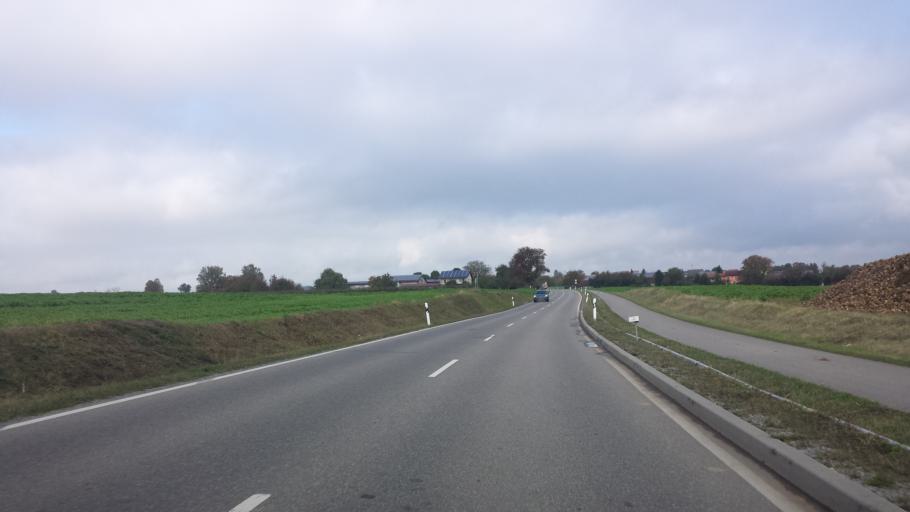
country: DE
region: Baden-Wuerttemberg
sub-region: Regierungsbezirk Stuttgart
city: Bad Rappenau
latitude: 49.2248
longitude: 9.1074
